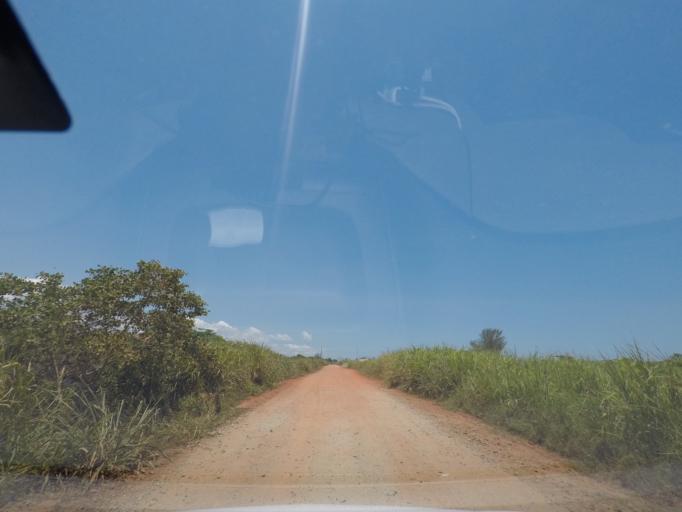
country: BR
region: Rio de Janeiro
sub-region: Niteroi
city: Niteroi
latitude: -22.9681
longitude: -42.9941
